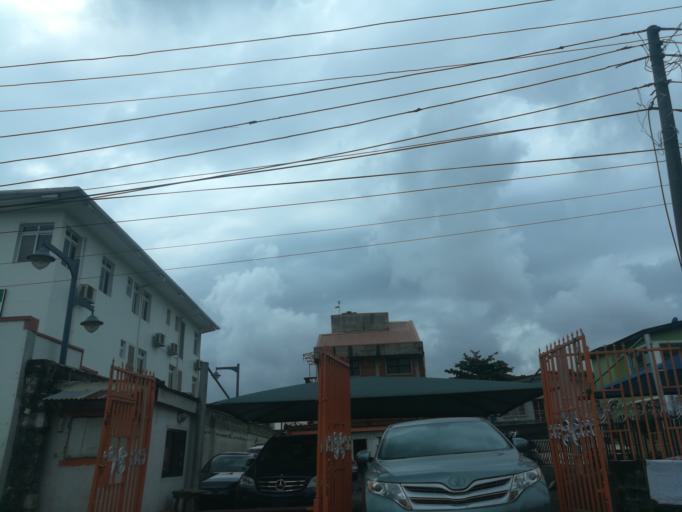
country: NG
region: Lagos
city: Ikeja
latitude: 6.6076
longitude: 3.3415
